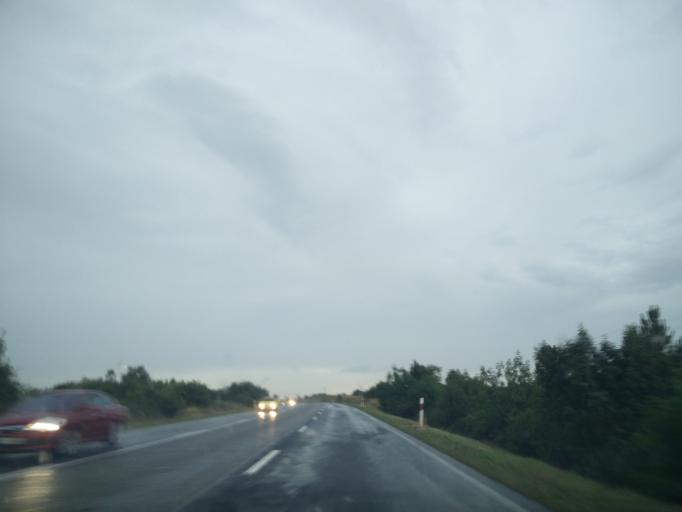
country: HU
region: Veszprem
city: Veszprem
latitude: 47.0915
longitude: 17.8772
